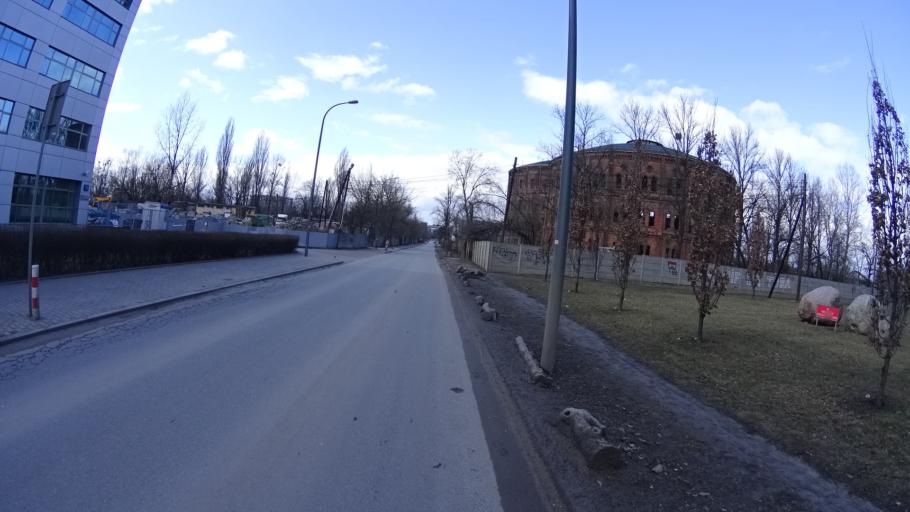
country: PL
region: Masovian Voivodeship
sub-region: Warszawa
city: Ochota
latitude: 52.2235
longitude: 20.9685
